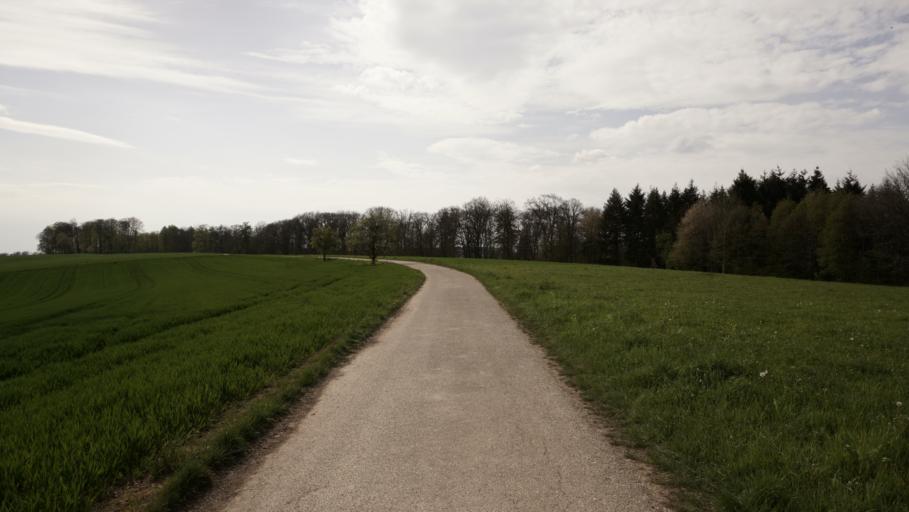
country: DE
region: Baden-Wuerttemberg
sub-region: Karlsruhe Region
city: Neckargerach
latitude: 49.4012
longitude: 9.0962
